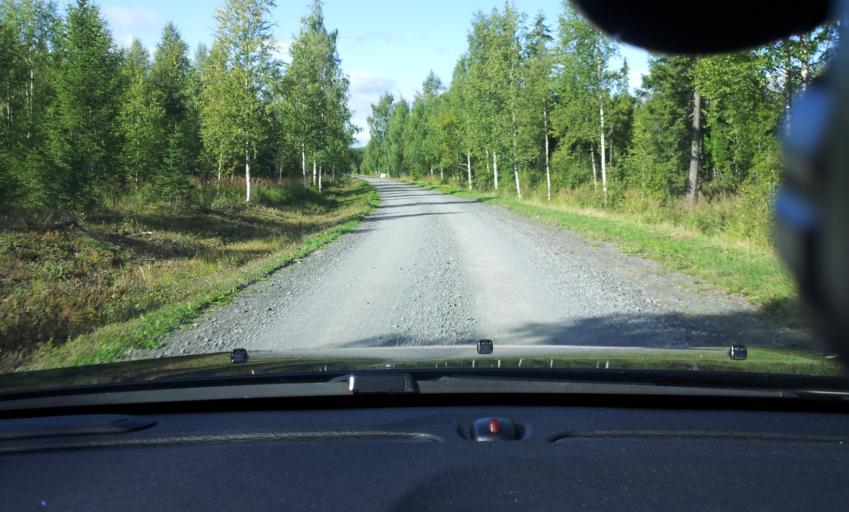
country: SE
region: Jaemtland
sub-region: Krokoms Kommun
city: Valla
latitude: 63.2637
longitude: 13.7925
